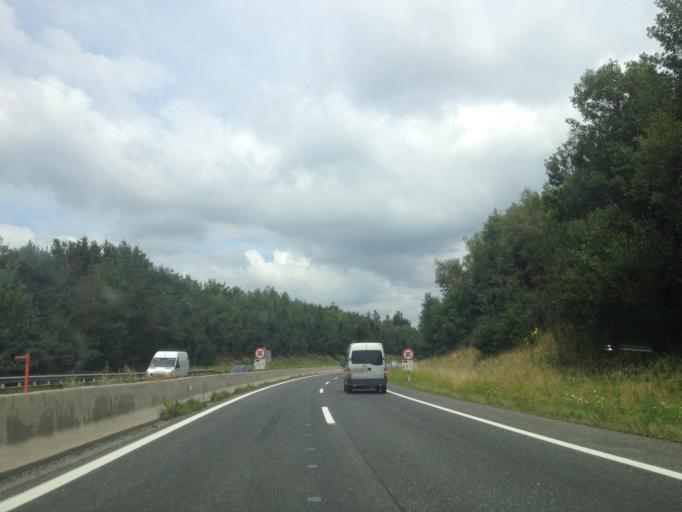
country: AT
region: Lower Austria
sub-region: Politischer Bezirk Neunkirchen
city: Zobern
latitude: 47.5356
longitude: 16.1105
